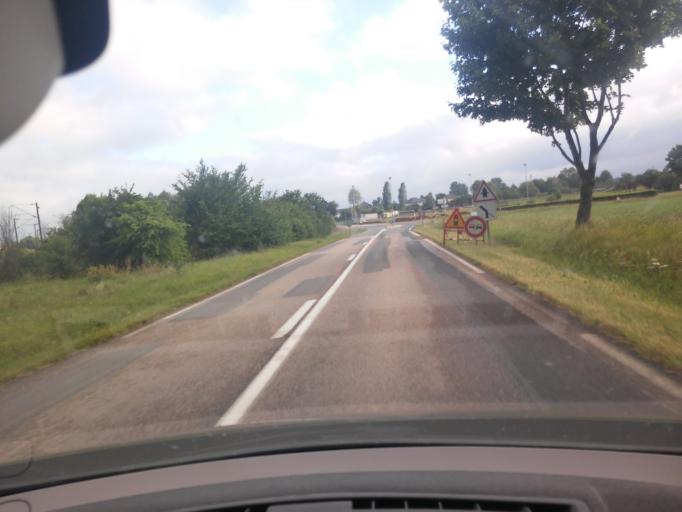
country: FR
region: Lorraine
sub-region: Departement de Meurthe-et-Moselle
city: Doncourt-les-Conflans
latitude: 49.0911
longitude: 5.8925
